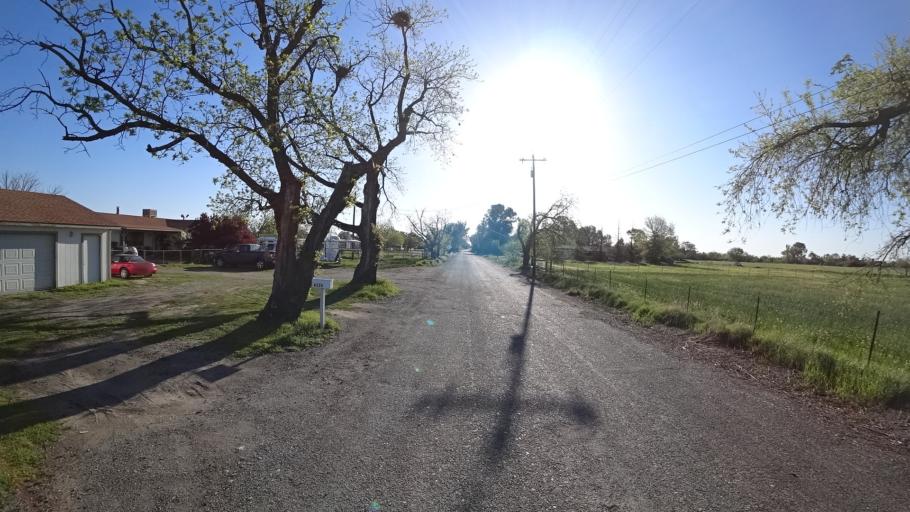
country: US
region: California
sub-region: Glenn County
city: Orland
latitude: 39.7696
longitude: -122.2284
